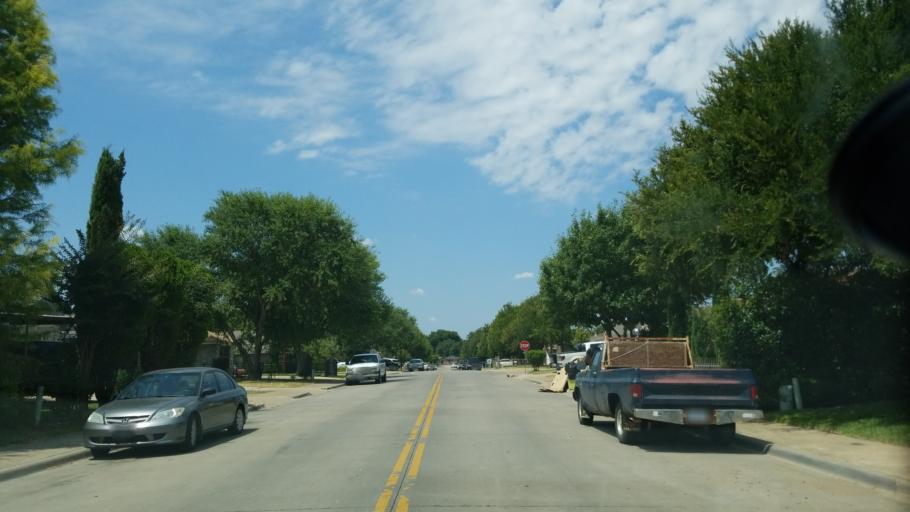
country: US
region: Texas
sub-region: Dallas County
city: Cockrell Hill
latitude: 32.7280
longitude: -96.8942
